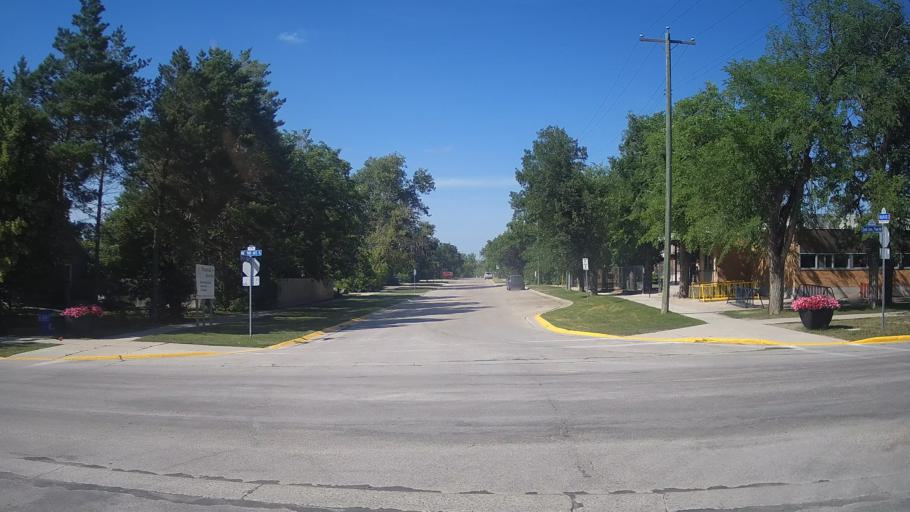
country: CA
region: Manitoba
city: Stonewall
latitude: 50.1375
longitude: -97.3266
